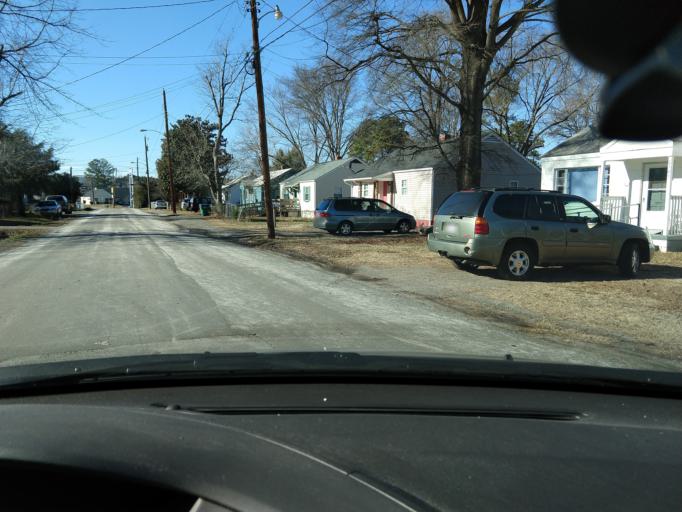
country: US
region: Virginia
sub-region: Chesterfield County
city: Bensley
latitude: 37.4662
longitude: -77.4410
